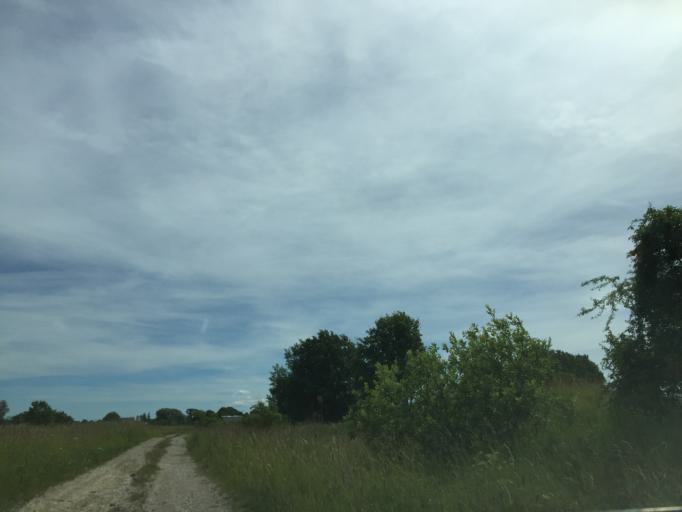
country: LV
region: Dundaga
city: Dundaga
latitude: 57.6117
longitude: 22.4427
